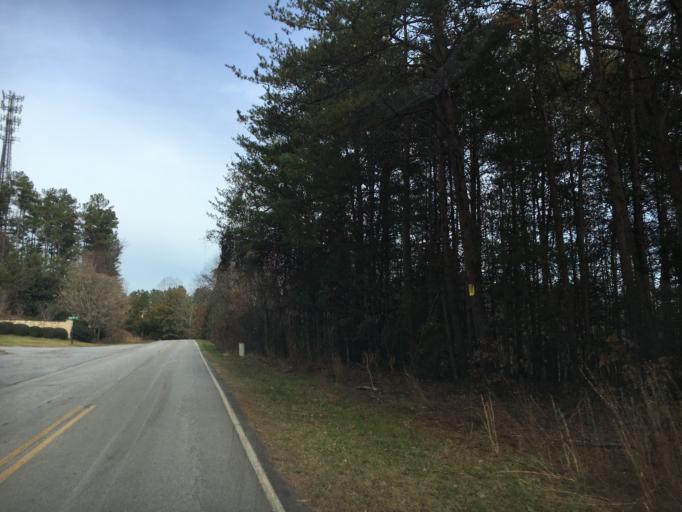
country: US
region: South Carolina
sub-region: Oconee County
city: Utica
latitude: 34.7715
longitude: -82.9092
